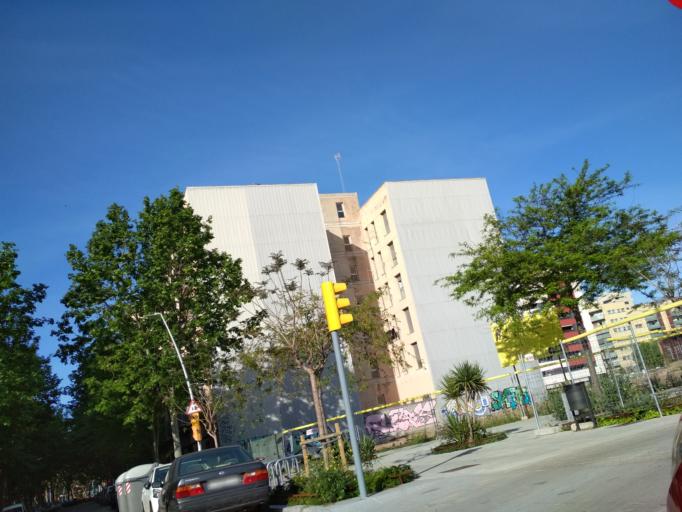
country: ES
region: Catalonia
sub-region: Provincia de Barcelona
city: Sant Marti
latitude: 41.4093
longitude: 2.2062
